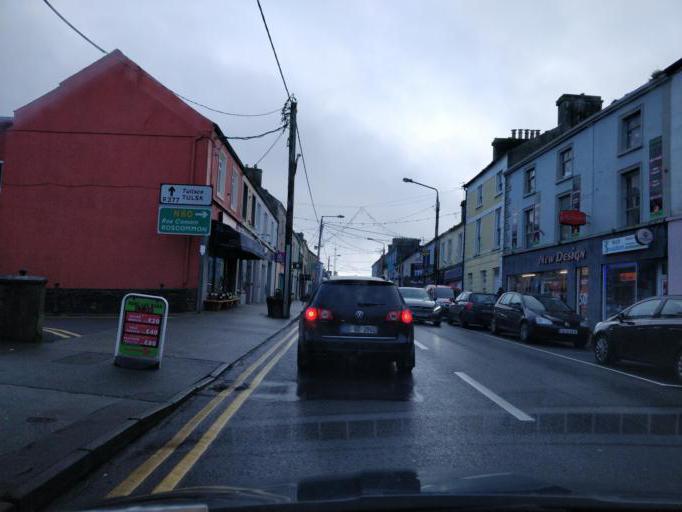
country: IE
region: Connaught
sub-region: Roscommon
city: Castlerea
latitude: 53.7675
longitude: -8.4888
